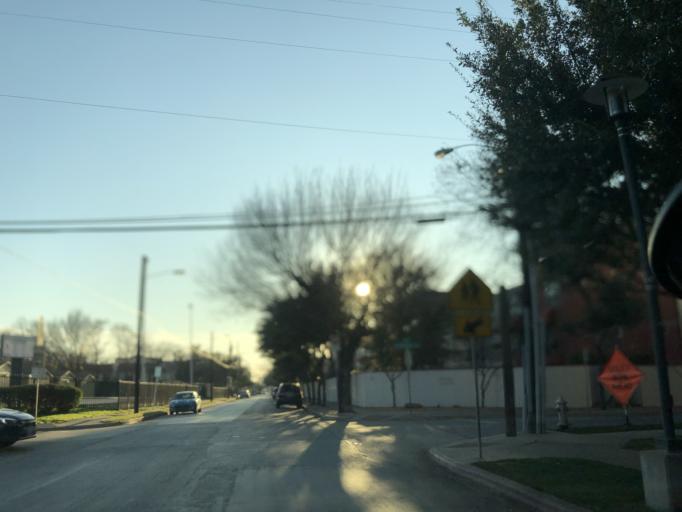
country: US
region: Texas
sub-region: Dallas County
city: Dallas
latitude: 32.8110
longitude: -96.8132
